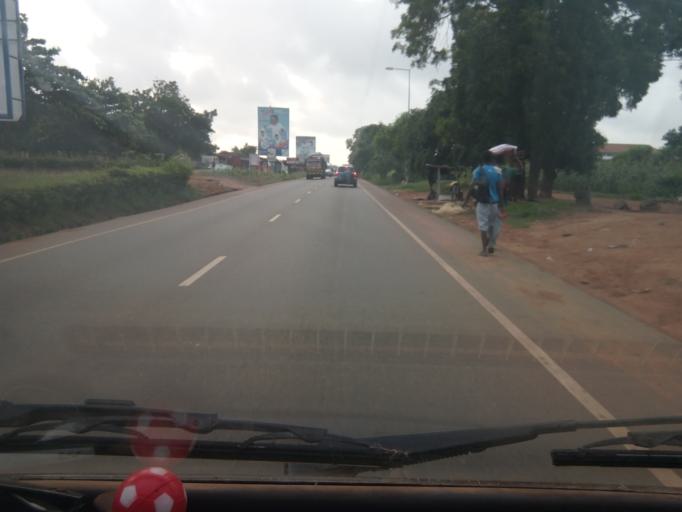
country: GH
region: Greater Accra
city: Medina Estates
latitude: 5.6674
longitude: -0.1853
